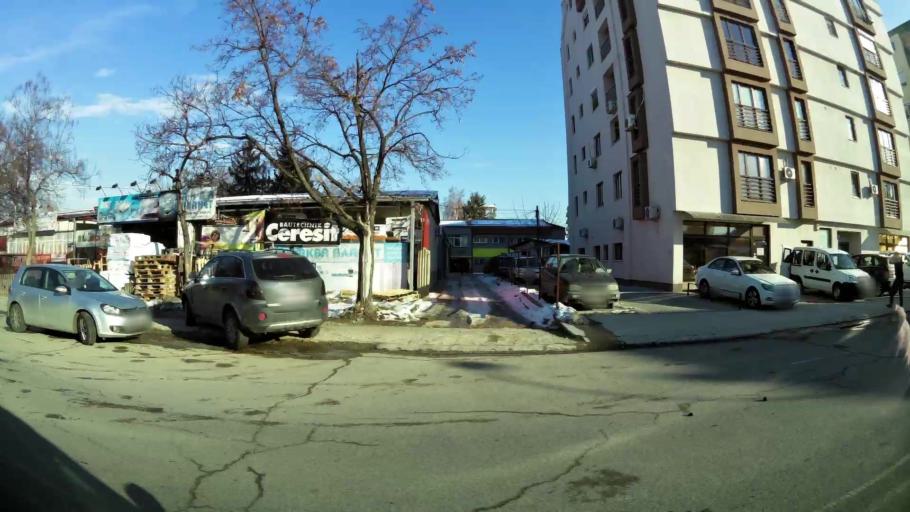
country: MK
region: Karpos
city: Skopje
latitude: 42.0010
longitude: 21.4011
